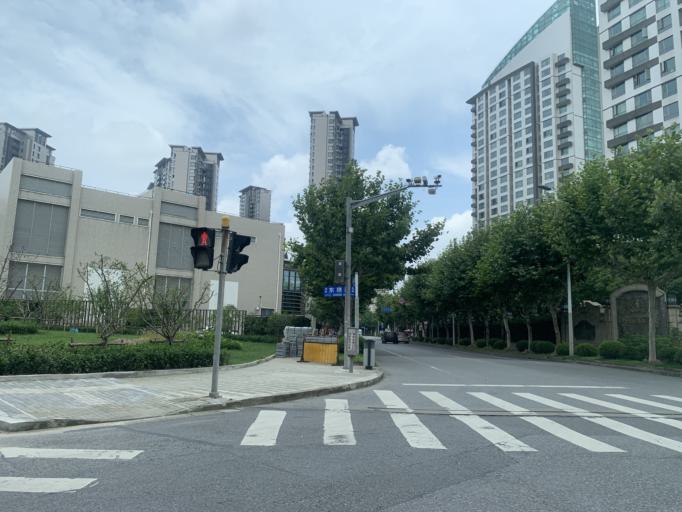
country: CN
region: Shanghai Shi
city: Huamu
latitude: 31.2112
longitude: 121.5330
